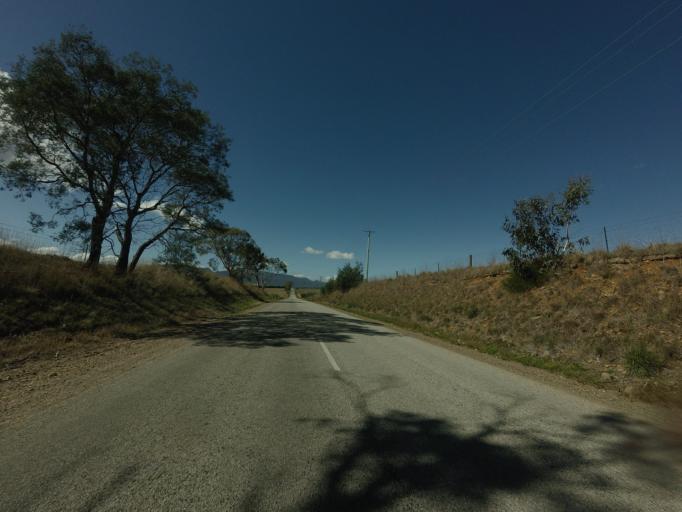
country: AU
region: Tasmania
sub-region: Break O'Day
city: St Helens
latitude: -41.6152
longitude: 148.0110
